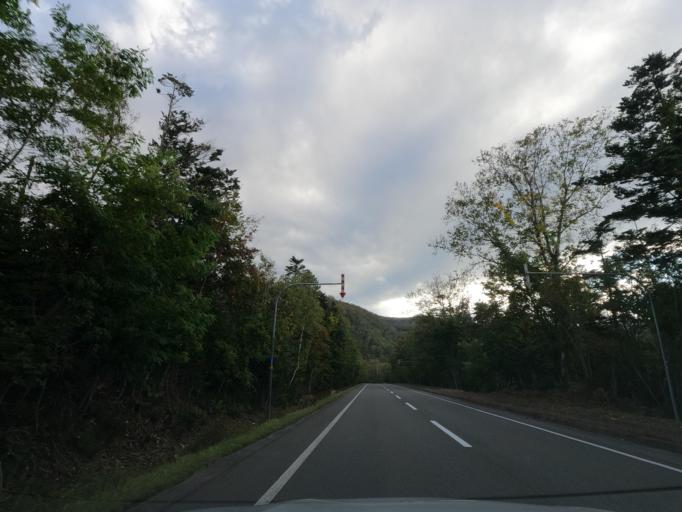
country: JP
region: Hokkaido
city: Shiraoi
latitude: 42.7078
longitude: 141.3115
